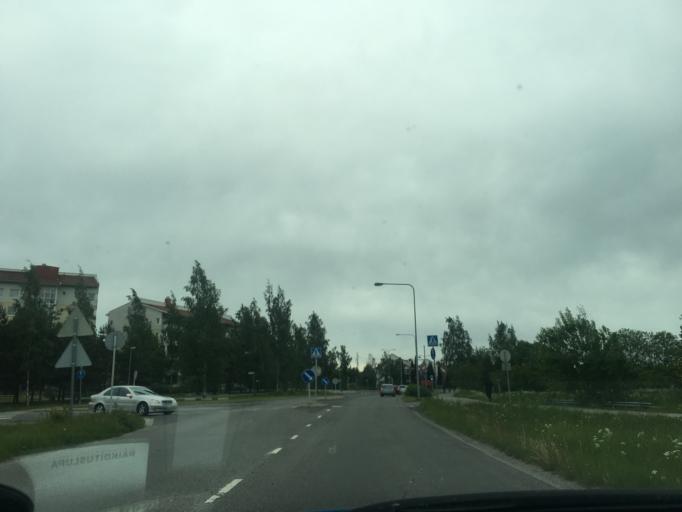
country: FI
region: Varsinais-Suomi
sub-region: Turku
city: Turku
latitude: 60.4719
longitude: 22.3086
